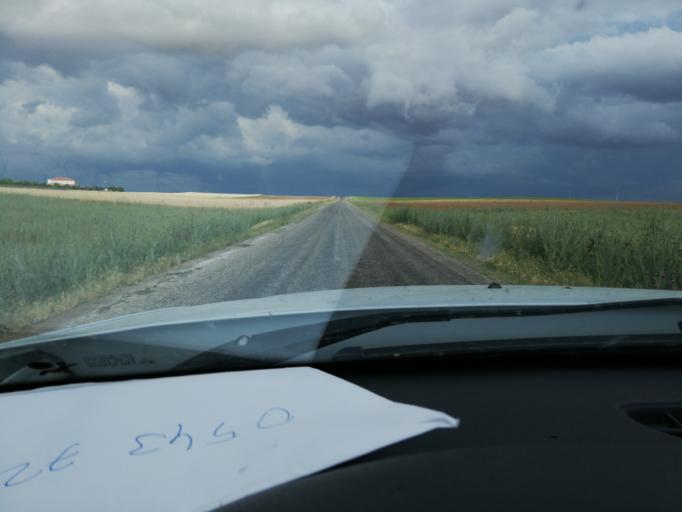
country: TR
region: Kirsehir
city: Kirsehir
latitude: 39.0420
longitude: 34.1701
